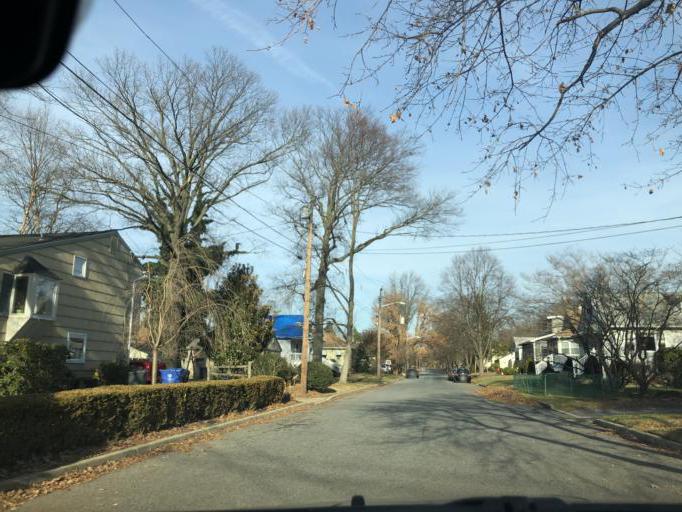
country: US
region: New Jersey
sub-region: Burlington County
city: Maple Shade
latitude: 39.9615
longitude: -74.9817
